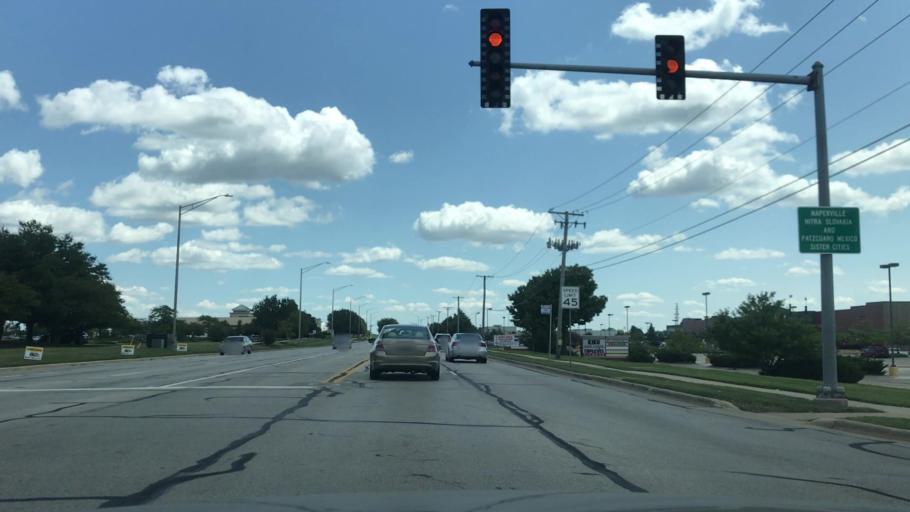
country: US
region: Illinois
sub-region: DuPage County
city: Naperville
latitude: 41.7627
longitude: -88.2011
